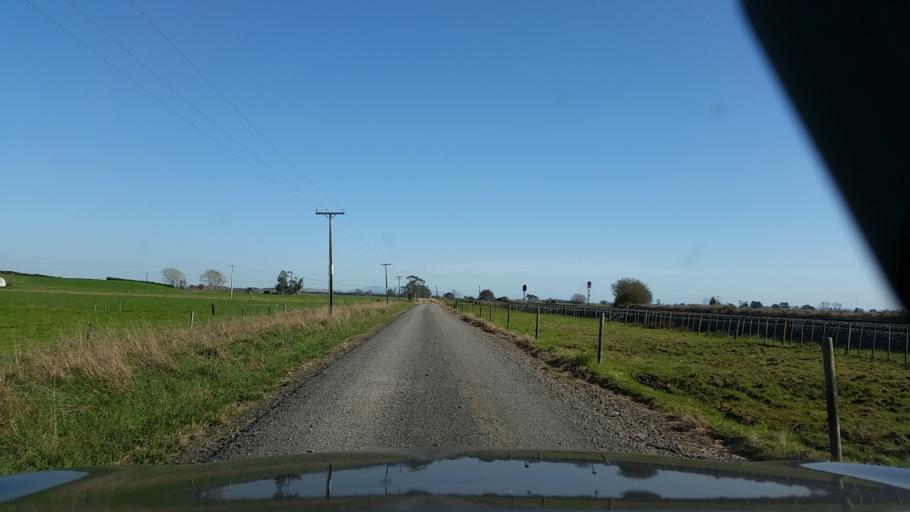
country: NZ
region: Waikato
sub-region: Waipa District
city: Cambridge
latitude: -37.6802
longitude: 175.4581
